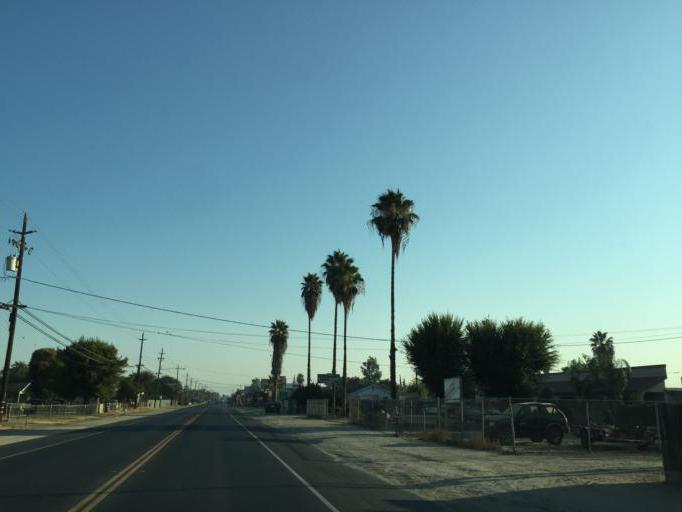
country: US
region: California
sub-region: Tulare County
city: Visalia
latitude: 36.3799
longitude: -119.2968
